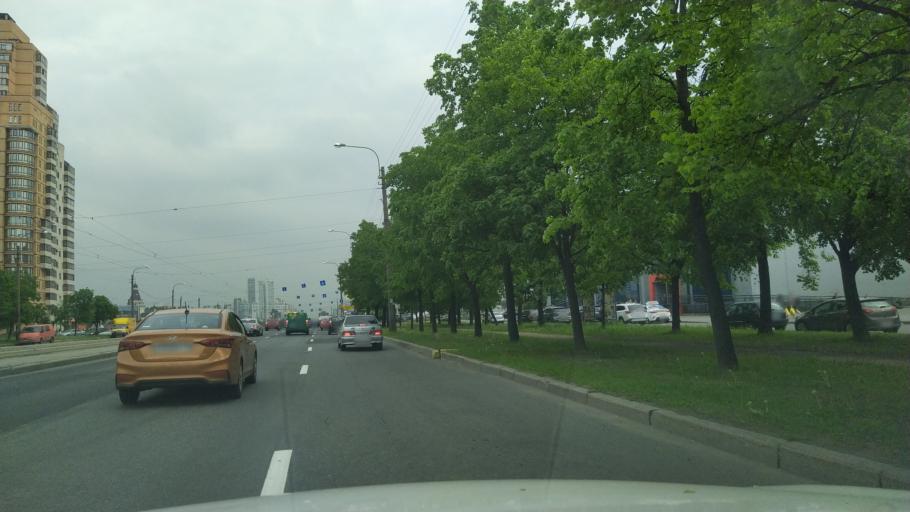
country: RU
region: St.-Petersburg
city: Kupchino
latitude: 59.8611
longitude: 30.3901
